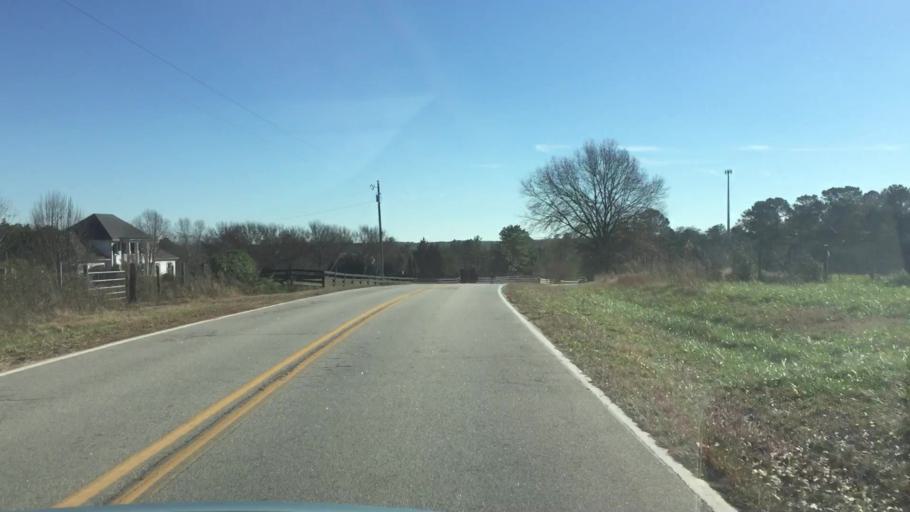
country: US
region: Georgia
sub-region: Newton County
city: Oakwood
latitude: 33.4953
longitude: -84.0473
